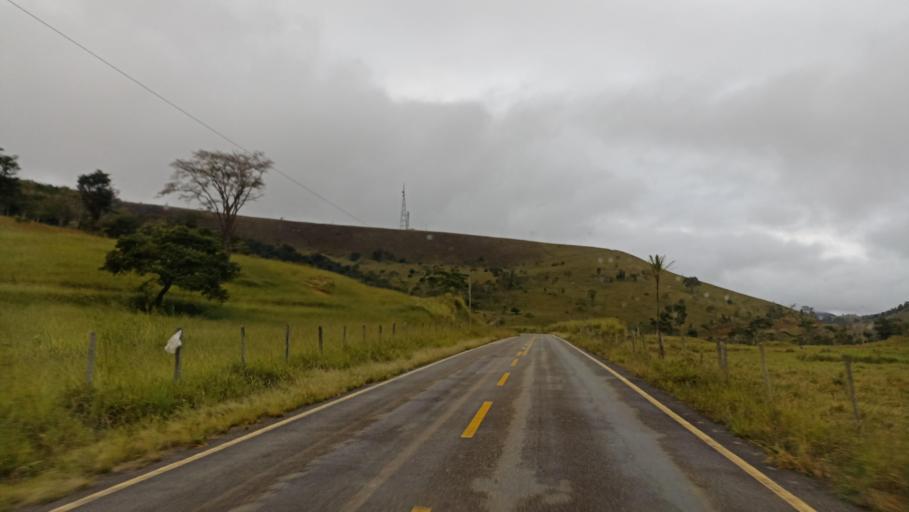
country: BR
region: Minas Gerais
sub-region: Joaima
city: Joaima
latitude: -16.6783
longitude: -40.5240
